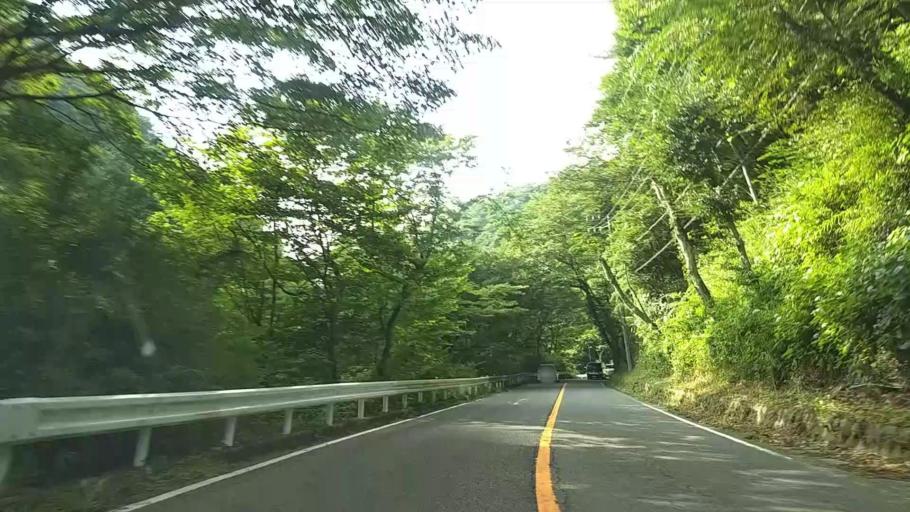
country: JP
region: Kanagawa
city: Hakone
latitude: 35.2607
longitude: 139.0283
